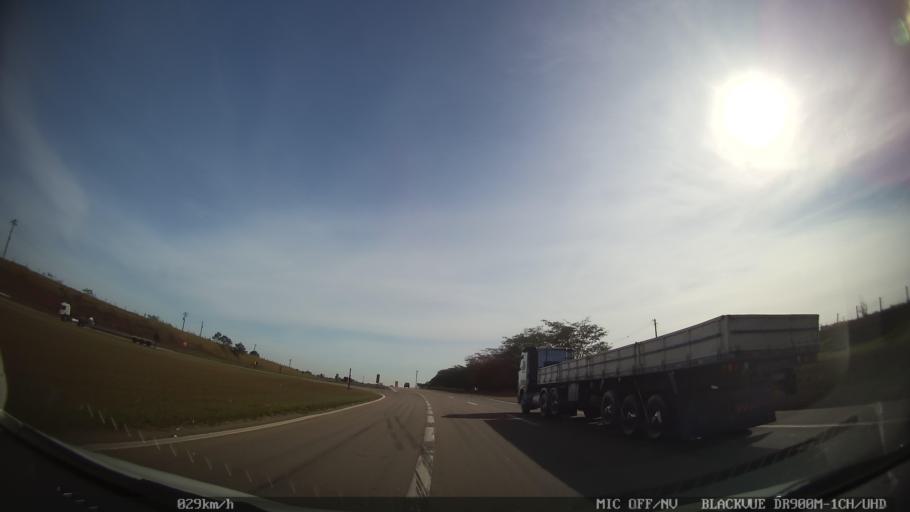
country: BR
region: Sao Paulo
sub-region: Rio Das Pedras
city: Rio das Pedras
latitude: -22.7931
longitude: -47.5815
